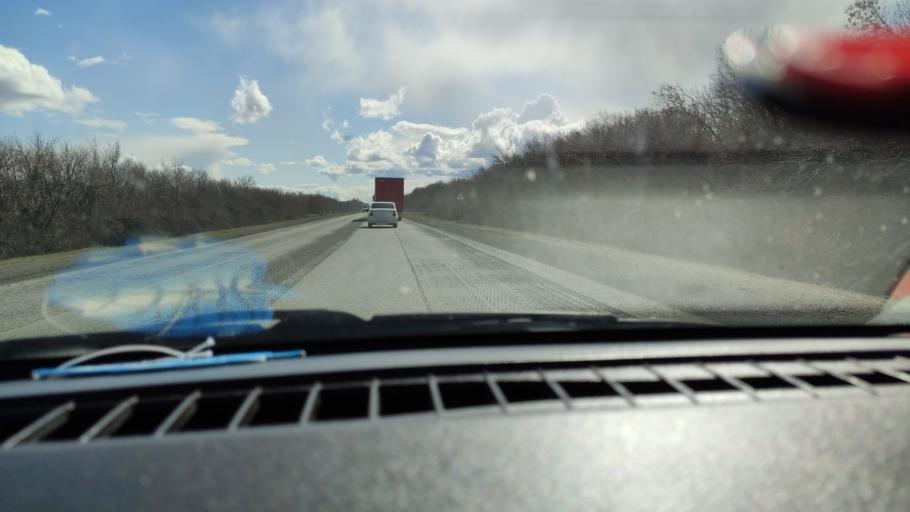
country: RU
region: Saratov
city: Dukhovnitskoye
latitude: 52.6453
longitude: 48.1953
